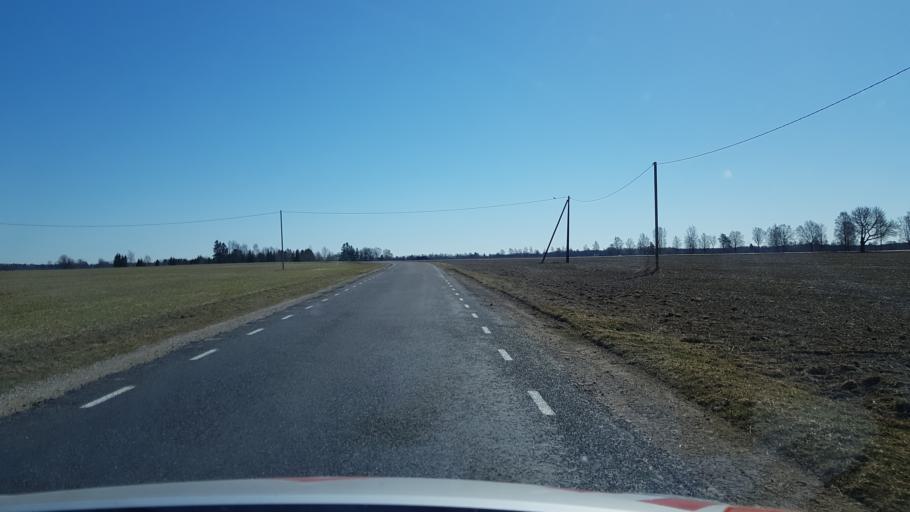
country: EE
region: Laeaene-Virumaa
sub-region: Haljala vald
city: Haljala
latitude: 59.4369
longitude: 26.1770
